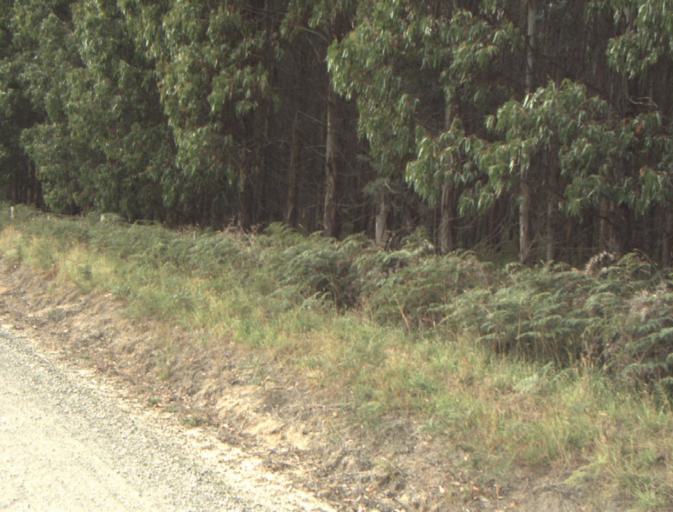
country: AU
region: Tasmania
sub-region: Dorset
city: Scottsdale
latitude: -41.3441
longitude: 147.4364
